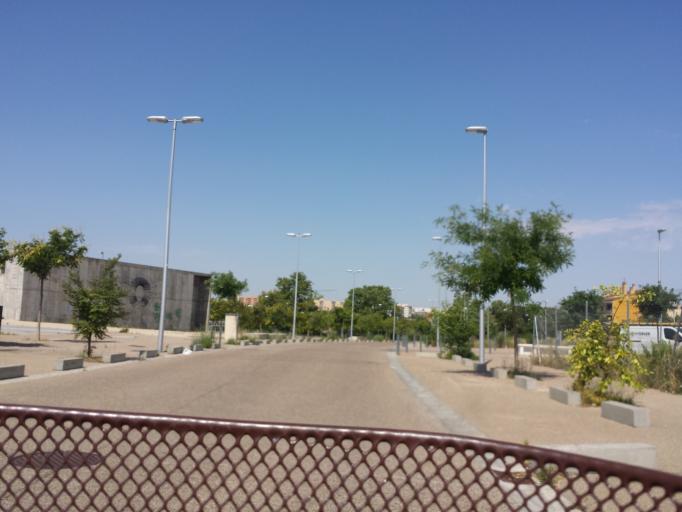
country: ES
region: Aragon
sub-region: Provincia de Zaragoza
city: Montecanal
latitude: 41.6349
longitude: -0.9319
